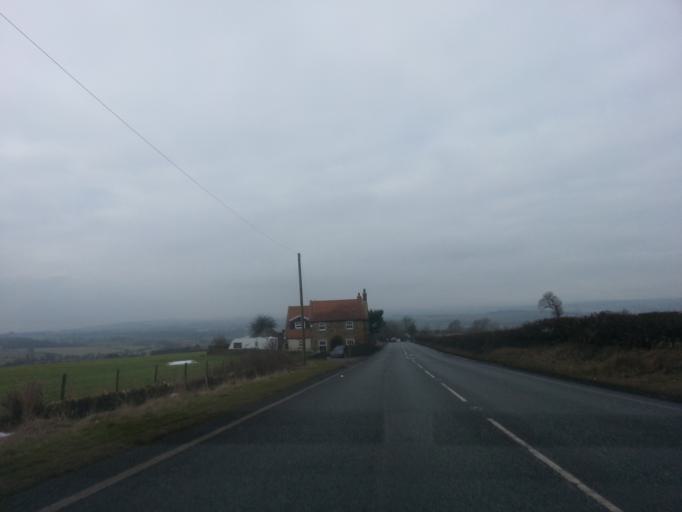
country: GB
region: England
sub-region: County Durham
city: Bishop Auckland
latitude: 54.6135
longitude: -1.6924
